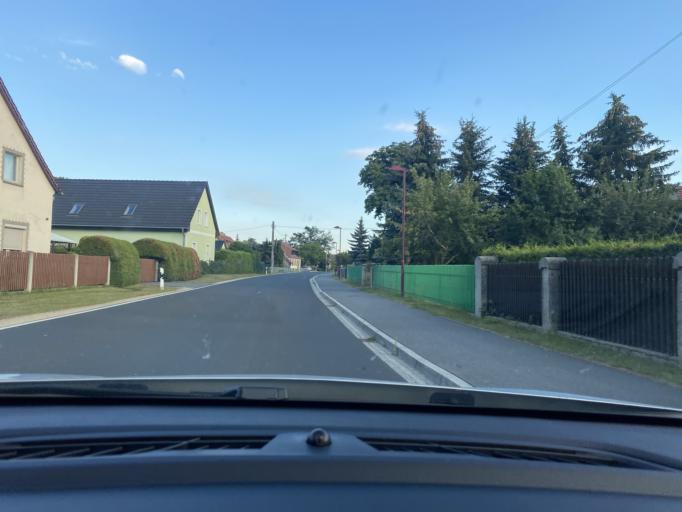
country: DE
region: Saxony
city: Kodersdorf
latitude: 51.2610
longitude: 14.8867
